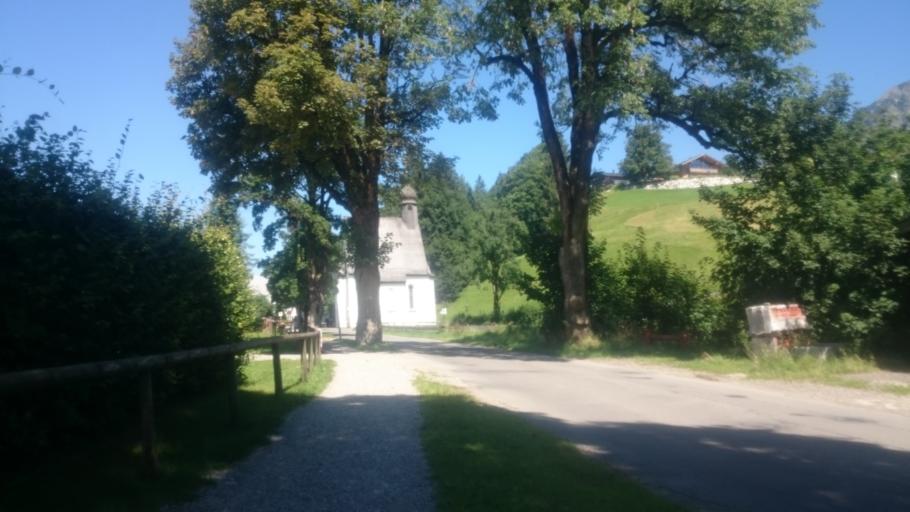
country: DE
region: Bavaria
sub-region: Swabia
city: Oberstdorf
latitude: 47.3955
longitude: 10.2811
